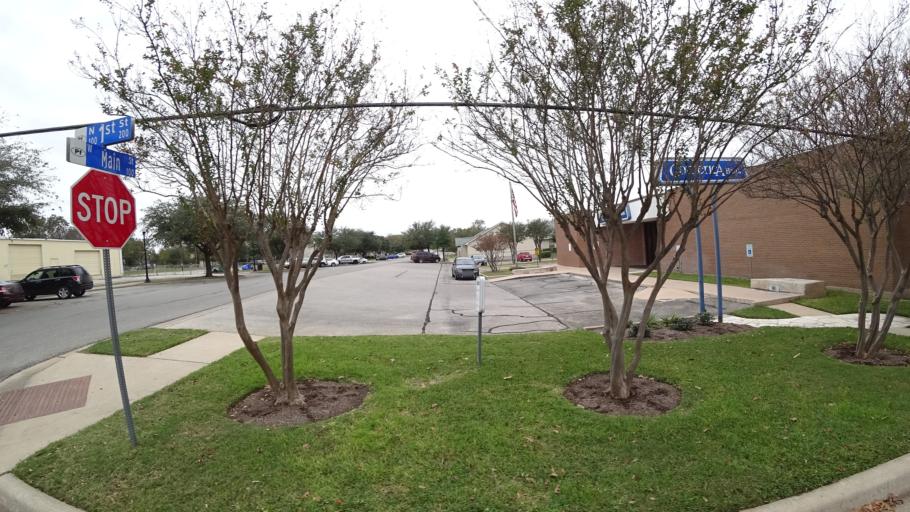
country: US
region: Texas
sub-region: Travis County
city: Pflugerville
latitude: 30.4409
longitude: -97.6203
